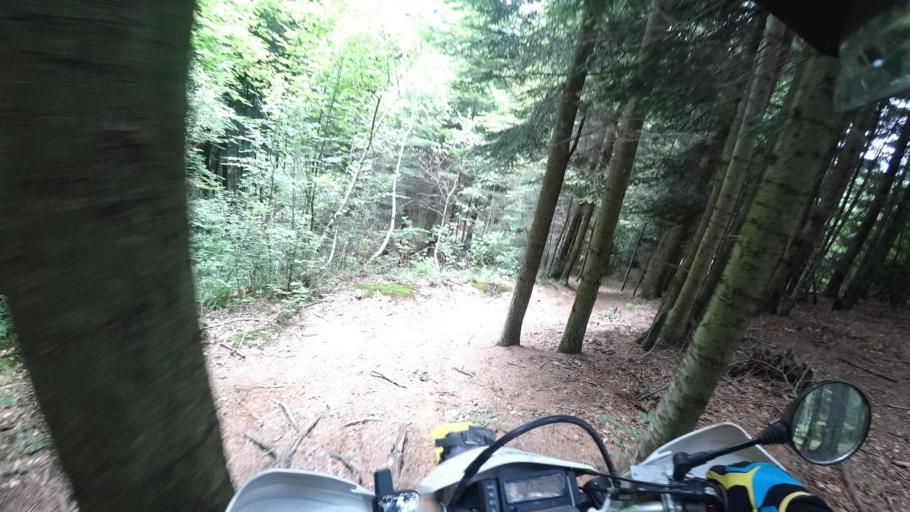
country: HR
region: Primorsko-Goranska
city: Hreljin
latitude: 45.2993
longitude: 14.7042
